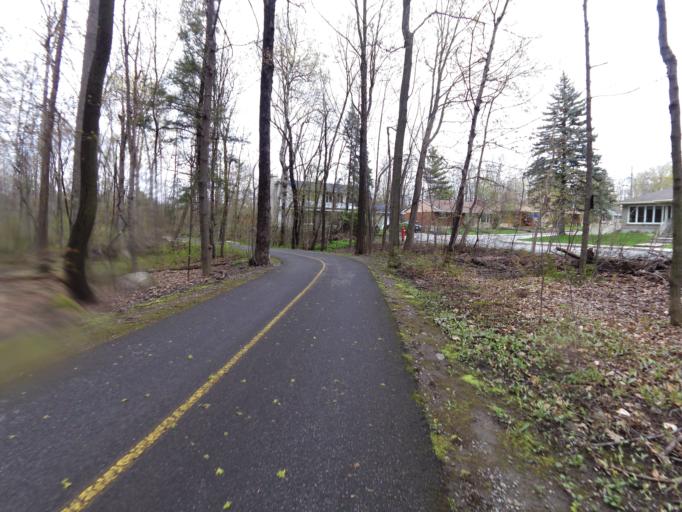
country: CA
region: Ontario
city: Ottawa
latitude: 45.4270
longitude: -75.7453
